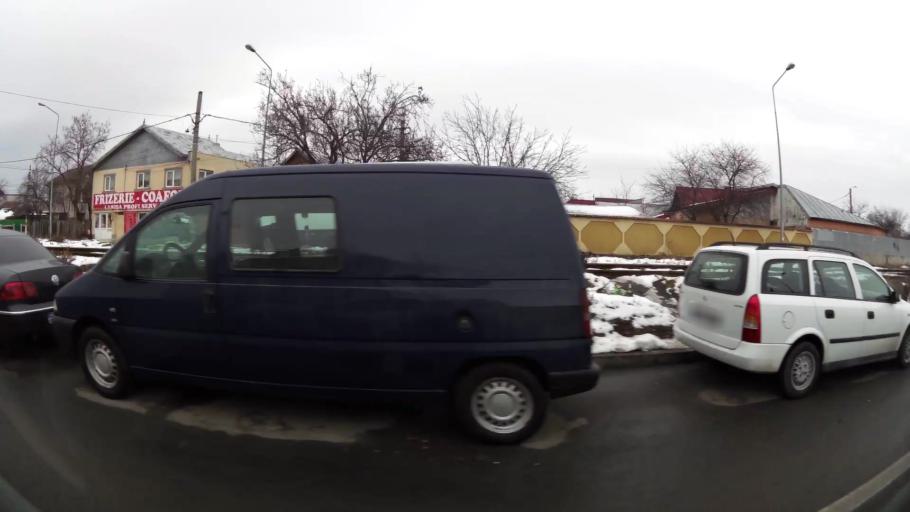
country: RO
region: Ilfov
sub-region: Comuna Pantelimon
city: Pantelimon
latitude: 44.4285
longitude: 26.2091
